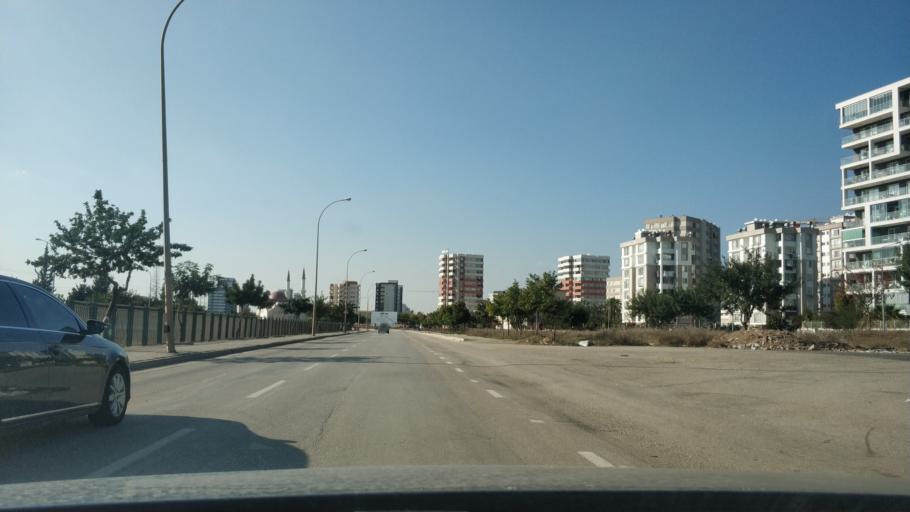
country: TR
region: Adana
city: Seyhan
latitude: 37.0095
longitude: 35.2679
